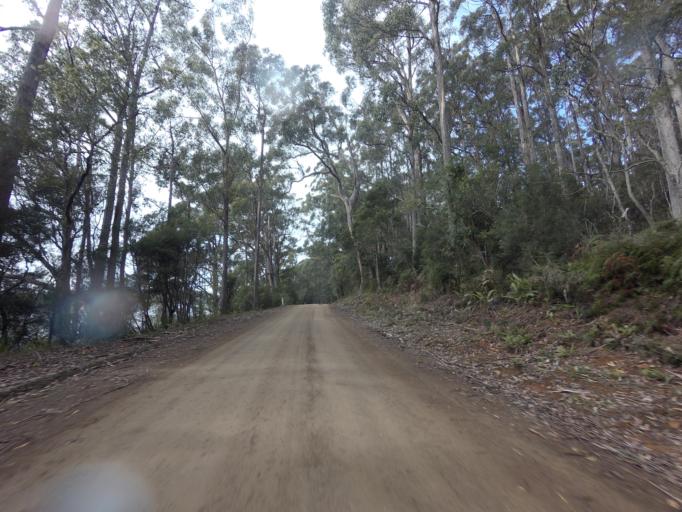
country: AU
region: Tasmania
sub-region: Huon Valley
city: Geeveston
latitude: -43.5675
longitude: 146.8883
